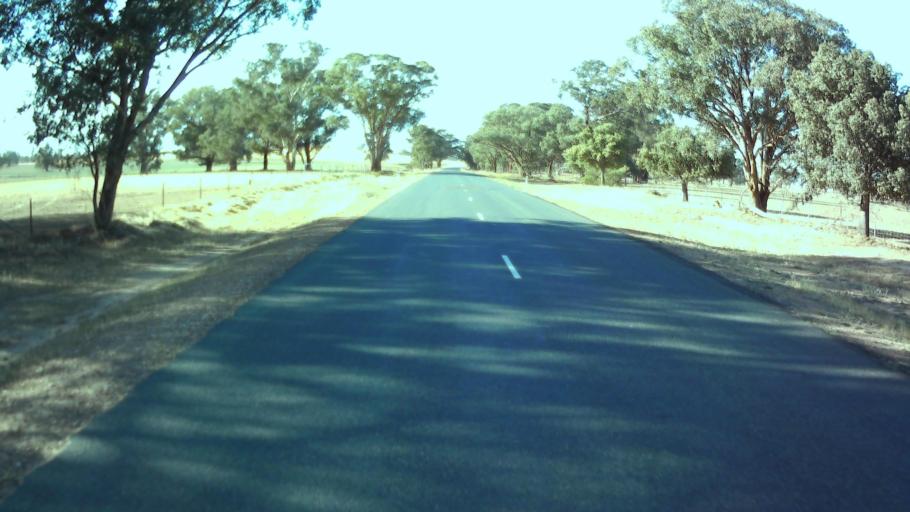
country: AU
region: New South Wales
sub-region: Weddin
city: Grenfell
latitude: -33.9631
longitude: 148.1403
